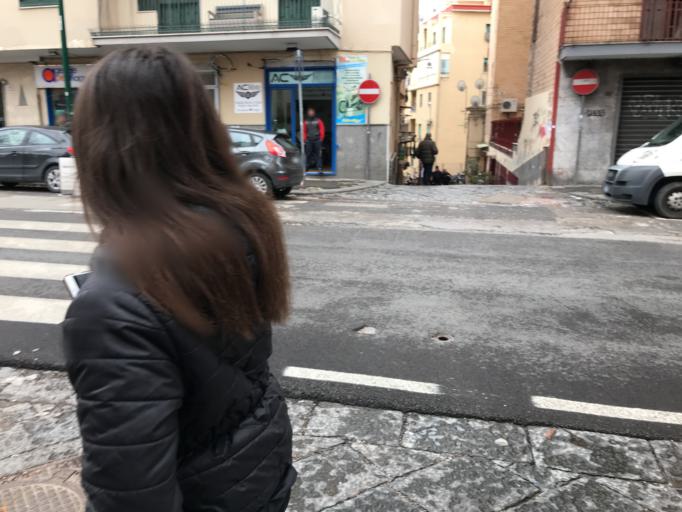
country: IT
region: Campania
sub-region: Provincia di Napoli
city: Napoli
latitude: 40.8554
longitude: 14.2298
